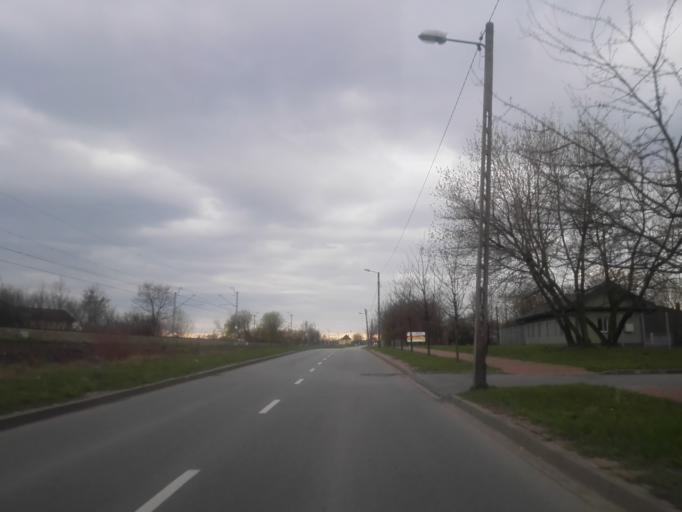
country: PL
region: Silesian Voivodeship
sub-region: Czestochowa
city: Czestochowa
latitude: 50.8310
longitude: 19.1418
